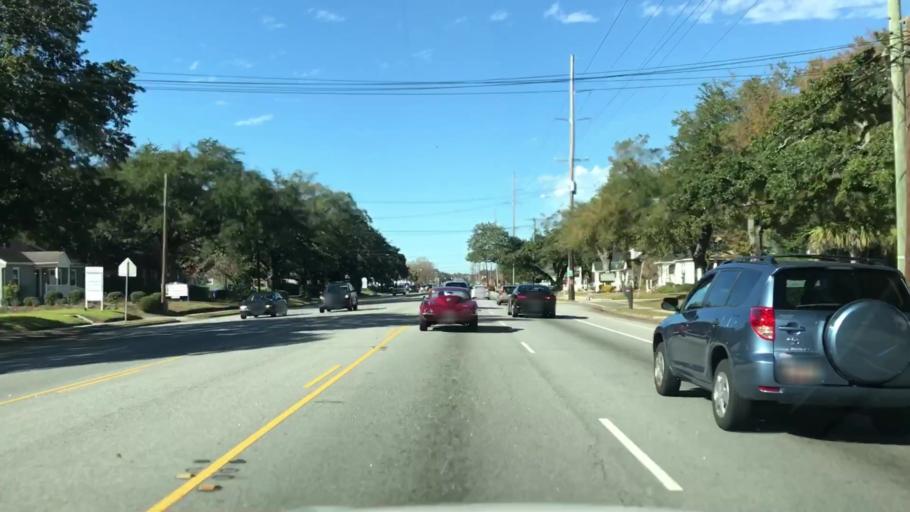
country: US
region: South Carolina
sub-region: Charleston County
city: Charleston
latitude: 32.7889
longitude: -79.9842
